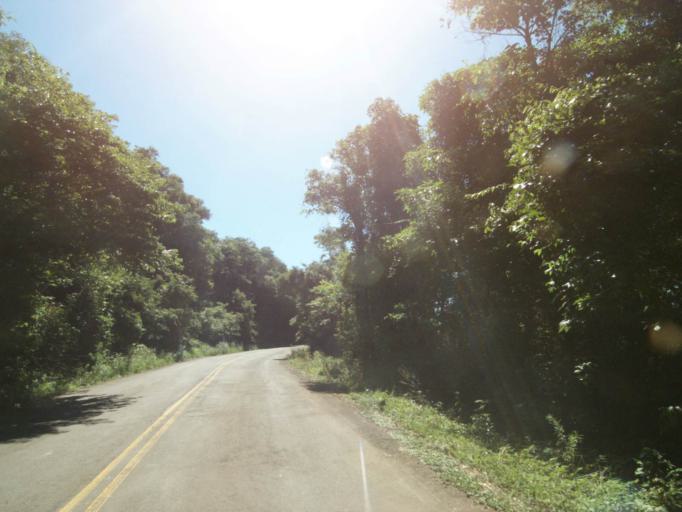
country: AR
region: Misiones
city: Bernardo de Irigoyen
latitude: -26.1872
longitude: -53.3614
